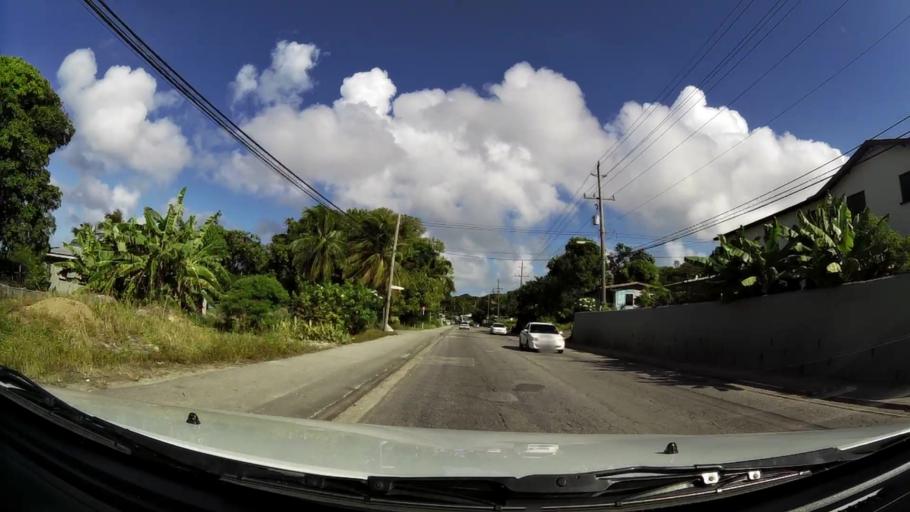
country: BB
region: Saint James
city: Holetown
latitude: 13.2218
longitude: -59.6217
